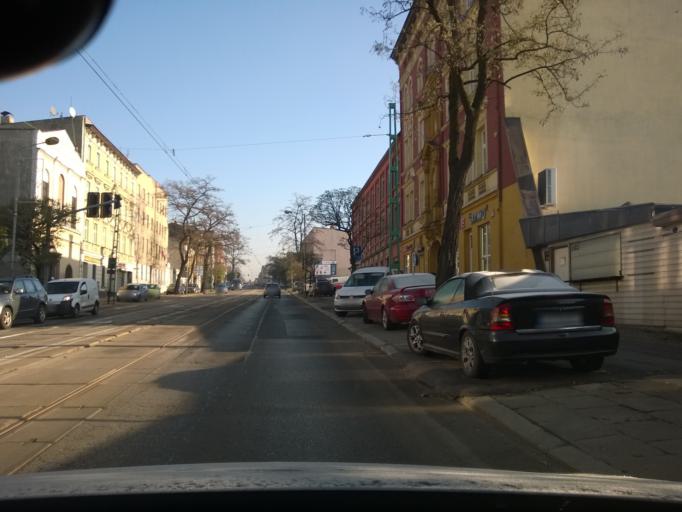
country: PL
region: Silesian Voivodeship
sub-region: Swietochlowice
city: Swietochlowice
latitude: 50.3026
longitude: 18.9401
